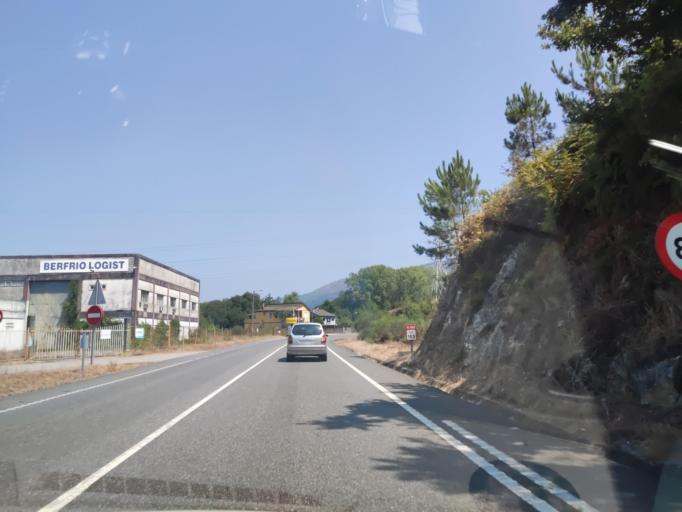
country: ES
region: Galicia
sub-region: Provincia de Pontevedra
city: Porrino
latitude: 42.1923
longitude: -8.6080
